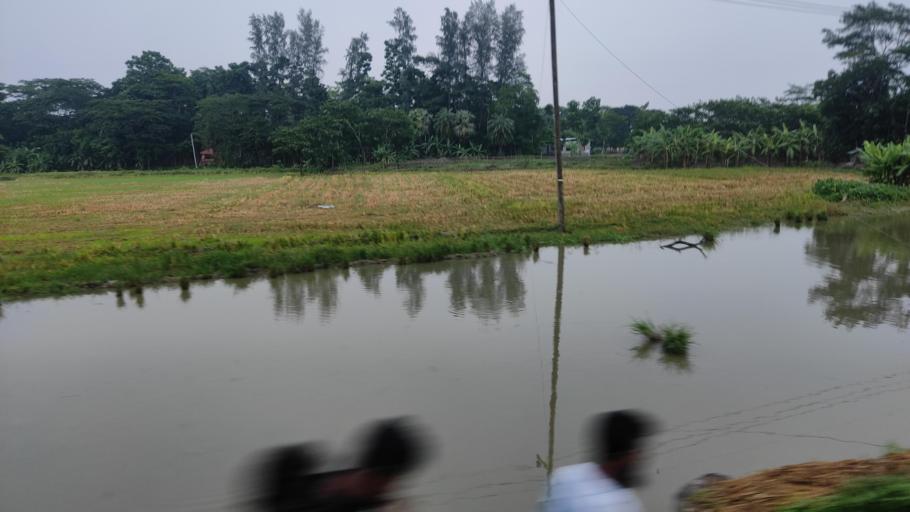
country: BD
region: Barisal
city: Bhandaria
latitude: 22.3195
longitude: 90.3258
